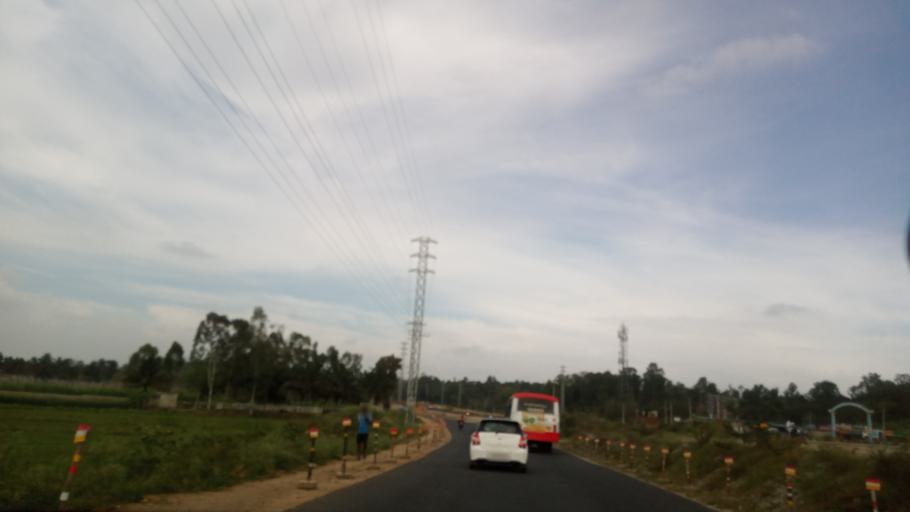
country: IN
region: Karnataka
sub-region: Mandya
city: Shrirangapattana
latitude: 12.4454
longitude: 76.7331
